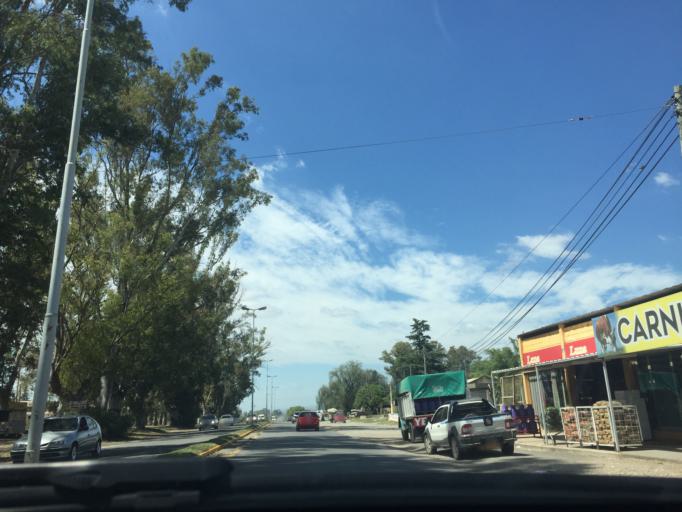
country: AR
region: Cordoba
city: Alta Gracia
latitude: -31.6602
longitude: -64.4098
